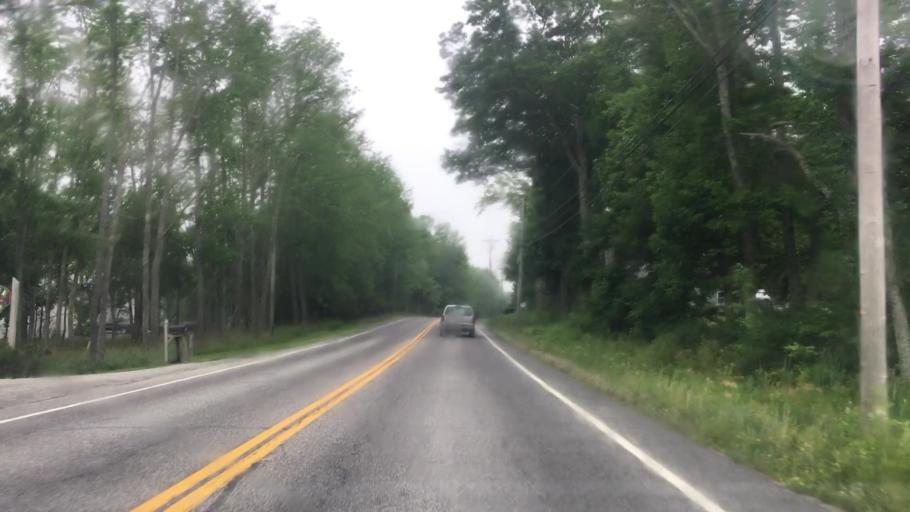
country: US
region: Maine
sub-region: Lincoln County
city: Edgecomb
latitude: 43.9245
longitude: -69.6163
